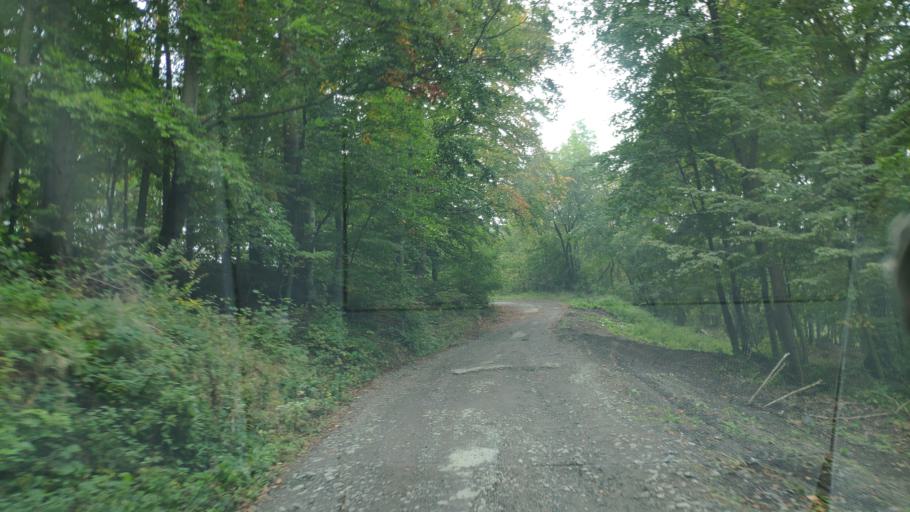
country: SK
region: Presovsky
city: Giraltovce
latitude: 48.9088
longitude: 21.4635
